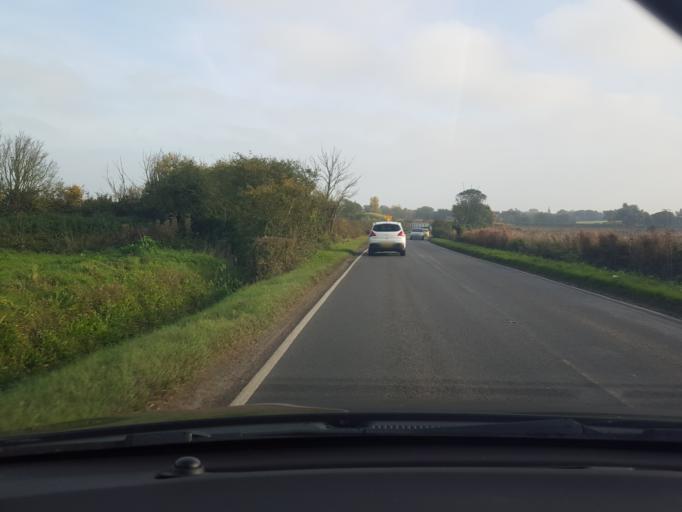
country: GB
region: England
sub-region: Essex
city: Frinton-on-Sea
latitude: 51.8559
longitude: 1.2115
